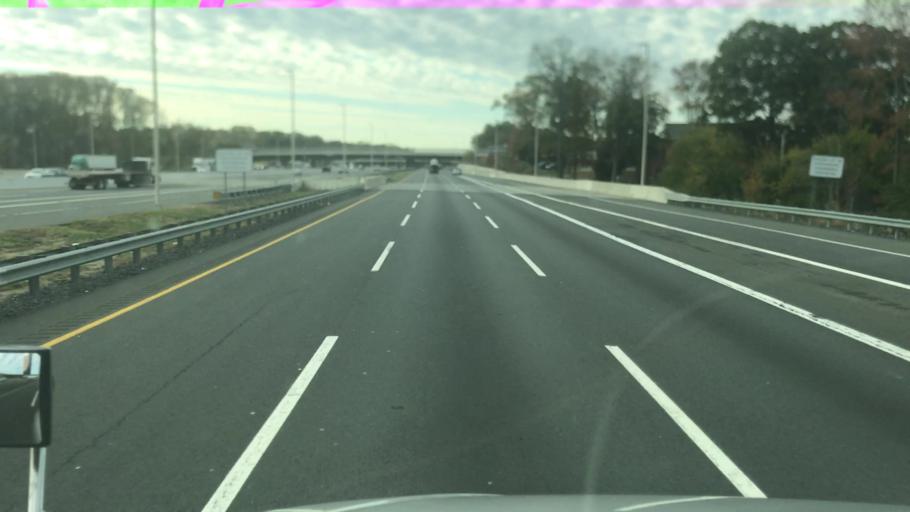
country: US
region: New Jersey
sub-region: Mercer County
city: Hightstown
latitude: 40.2614
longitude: -74.5129
